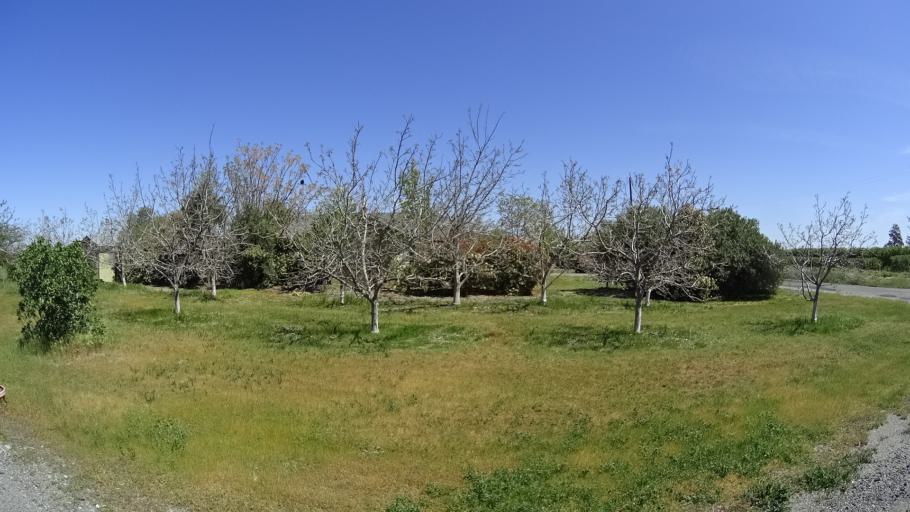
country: US
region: California
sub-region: Glenn County
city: Orland
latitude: 39.7399
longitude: -122.1595
